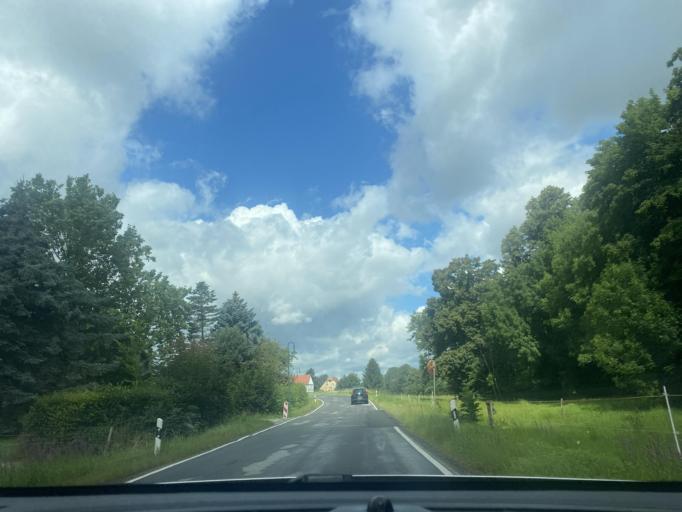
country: DE
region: Saxony
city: Sohland am Rotstein
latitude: 51.1295
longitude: 14.7779
